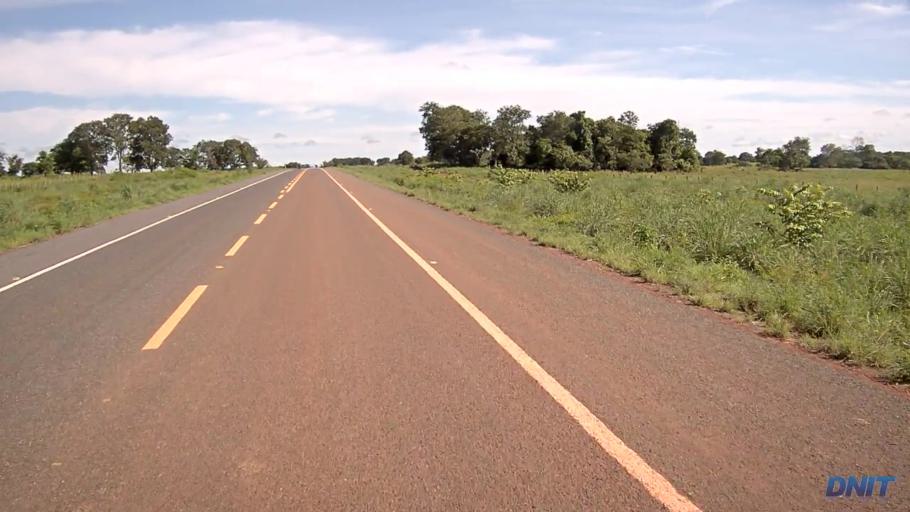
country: BR
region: Goias
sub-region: Sao Miguel Do Araguaia
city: Sao Miguel do Araguaia
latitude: -13.4706
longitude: -50.1149
